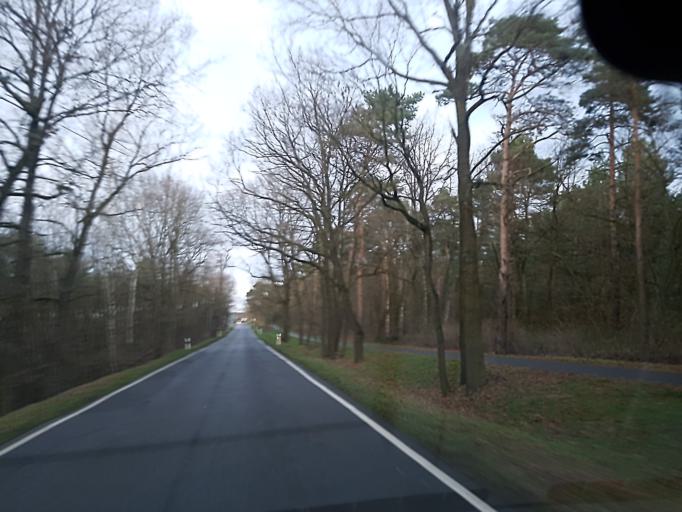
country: DE
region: Brandenburg
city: Elsterwerda
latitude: 51.4870
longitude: 13.5067
